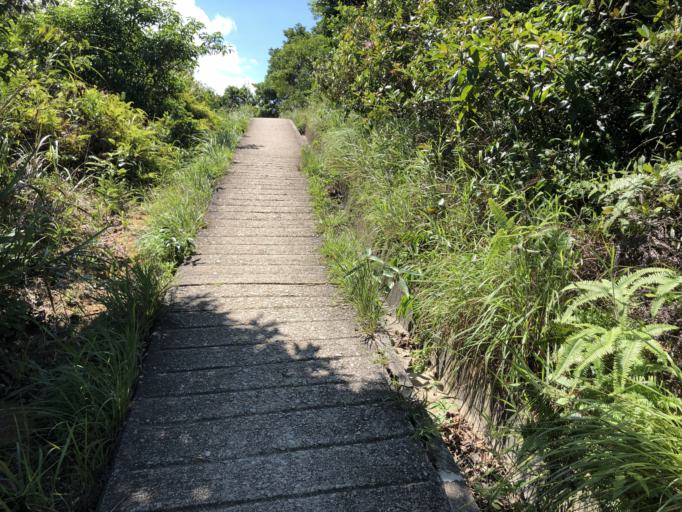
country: HK
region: Tuen Mun
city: Tuen Mun
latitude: 22.2807
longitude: 113.9847
